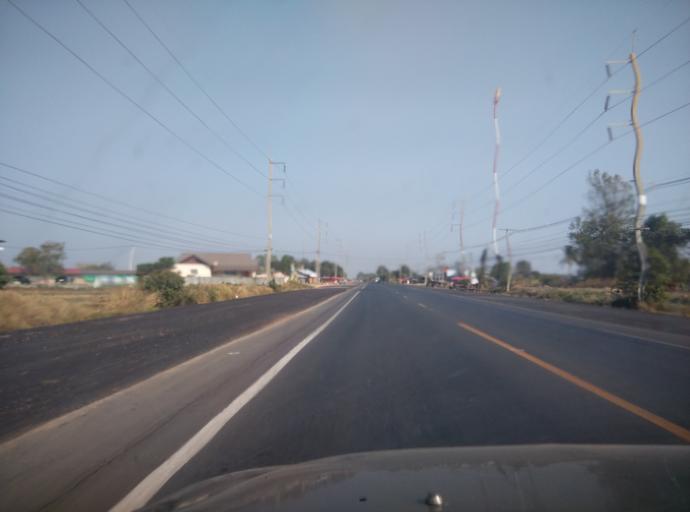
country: TH
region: Sisaket
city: Uthumphon Phisai
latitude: 15.1526
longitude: 104.2023
